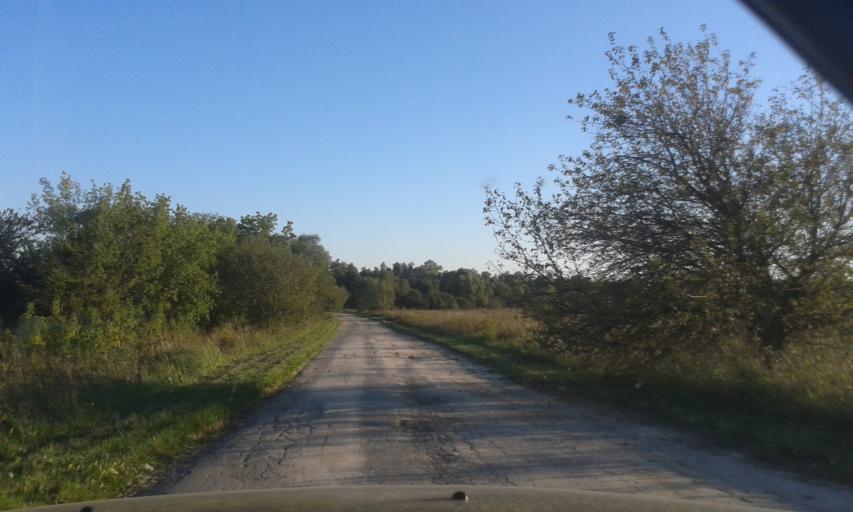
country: RU
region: Tula
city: Krapivna
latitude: 54.1230
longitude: 37.1537
